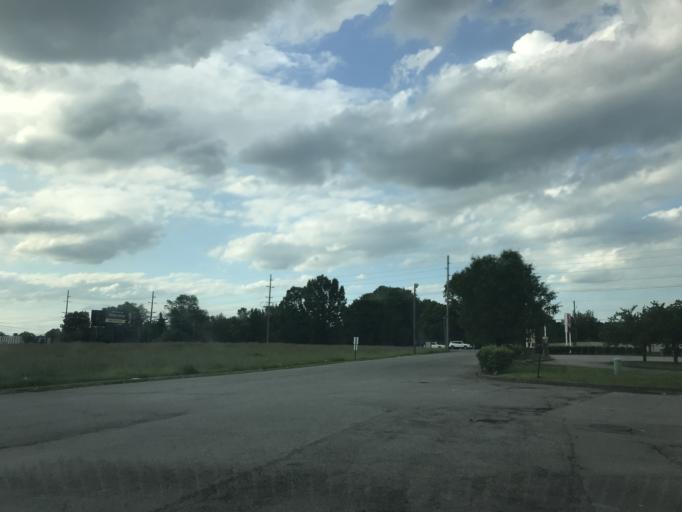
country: US
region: Kentucky
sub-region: Jefferson County
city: Buechel
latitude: 38.1785
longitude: -85.6245
